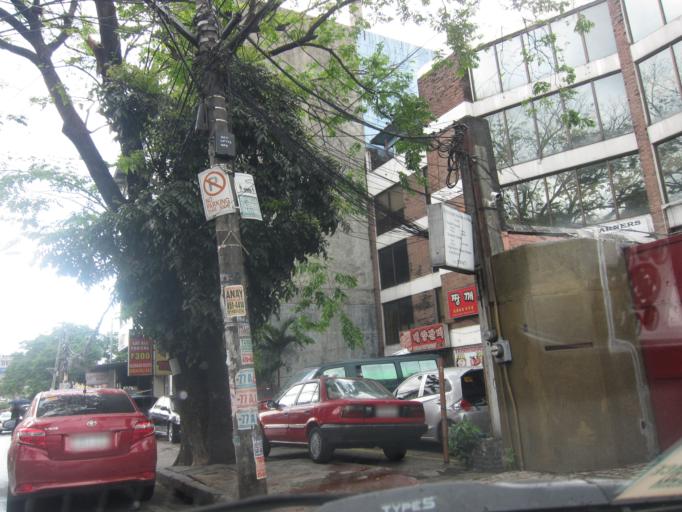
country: PH
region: Metro Manila
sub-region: Quezon City
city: Quezon City
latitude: 14.6434
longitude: 121.0540
